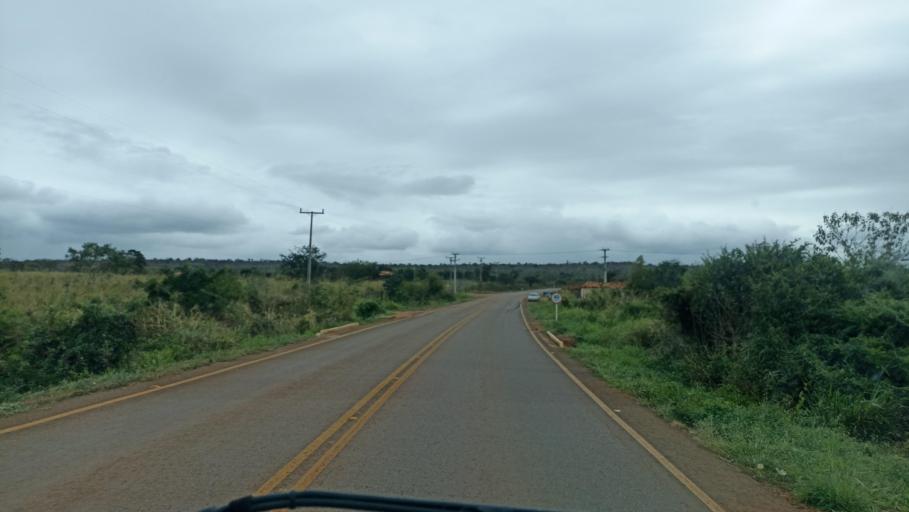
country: BR
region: Bahia
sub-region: Andarai
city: Vera Cruz
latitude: -13.0046
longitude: -40.9837
